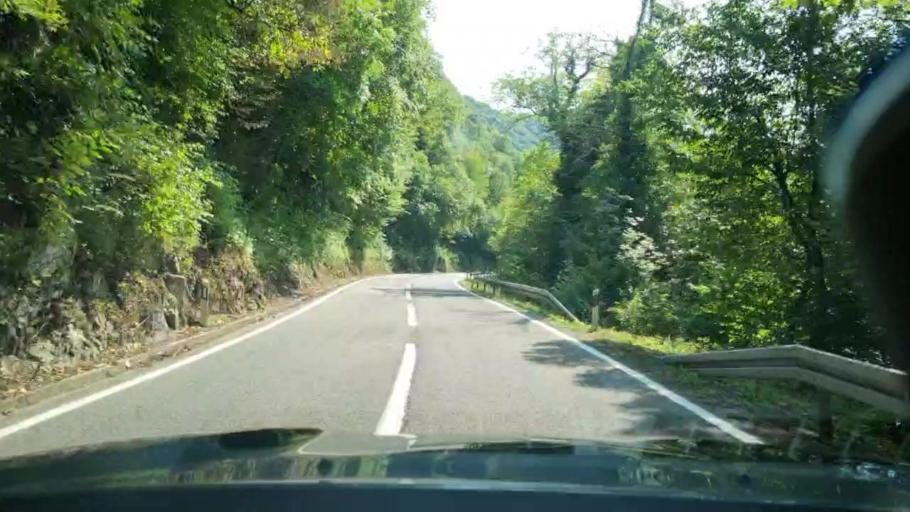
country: BA
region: Federation of Bosnia and Herzegovina
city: Bosanska Krupa
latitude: 44.8726
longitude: 16.1119
